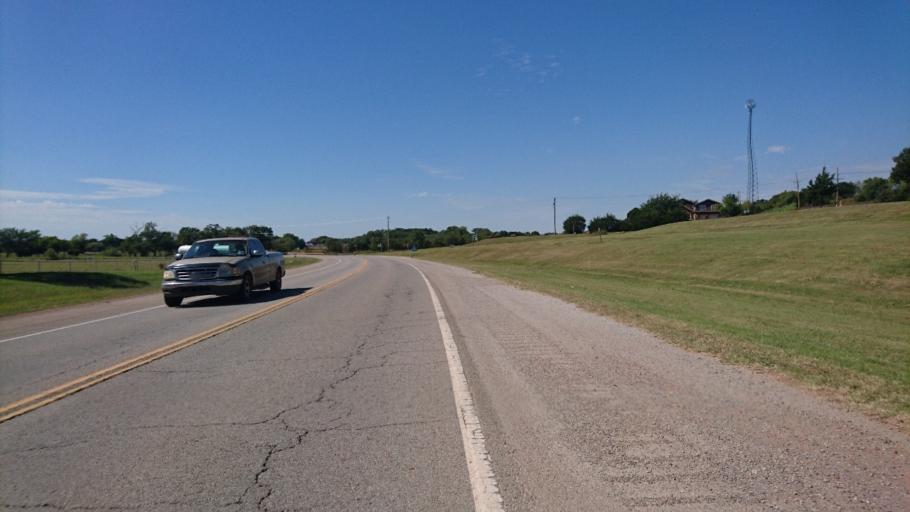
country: US
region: Oklahoma
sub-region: Oklahoma County
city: Jones
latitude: 35.6666
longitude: -97.3163
